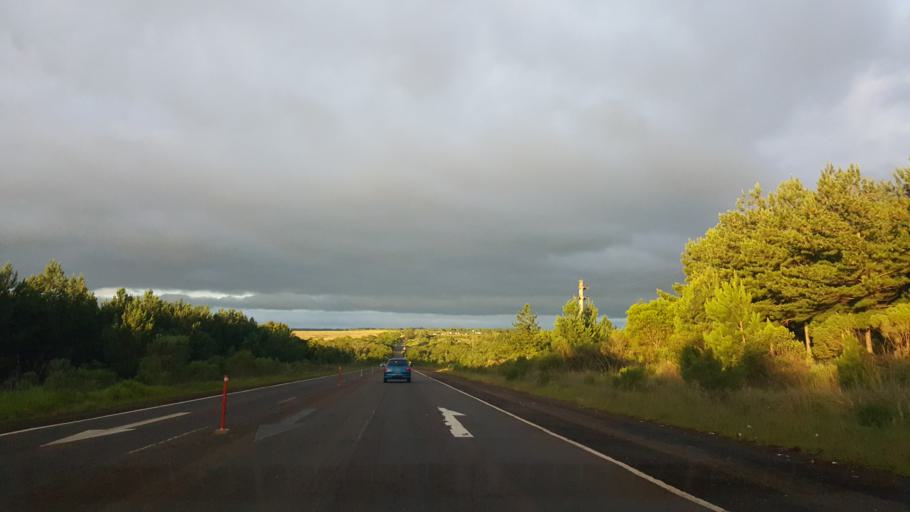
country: AR
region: Misiones
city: Cerro Cora
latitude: -27.4469
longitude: -55.6510
